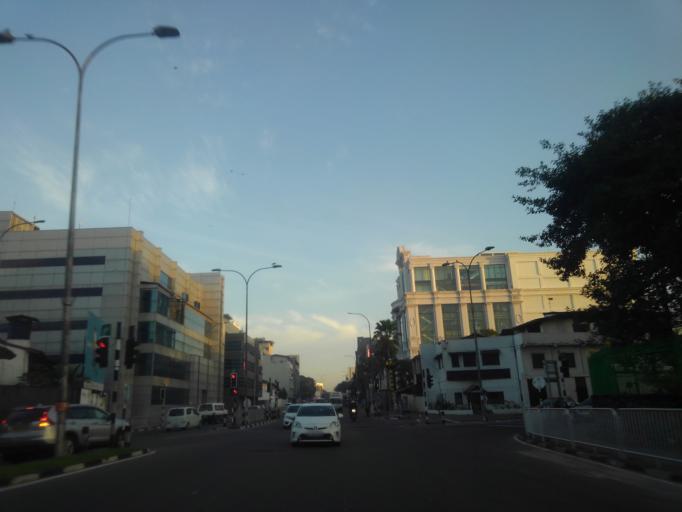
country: LK
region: Western
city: Kolonnawa
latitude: 6.9090
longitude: 79.8775
